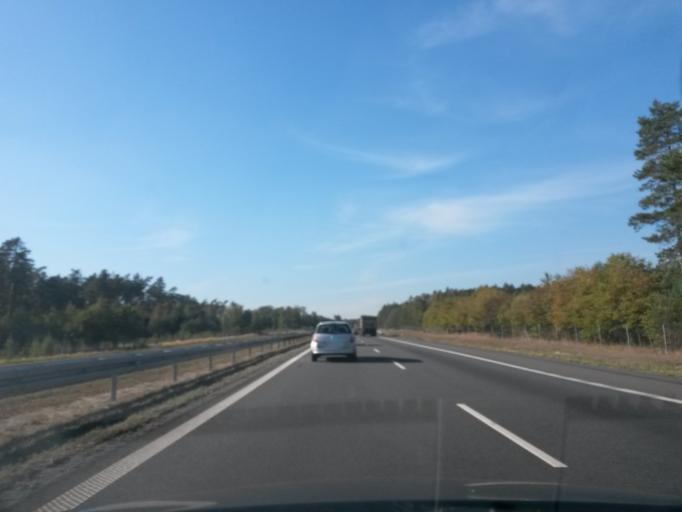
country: PL
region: Opole Voivodeship
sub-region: Powiat opolski
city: Komprachcice
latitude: 50.5890
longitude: 17.8132
